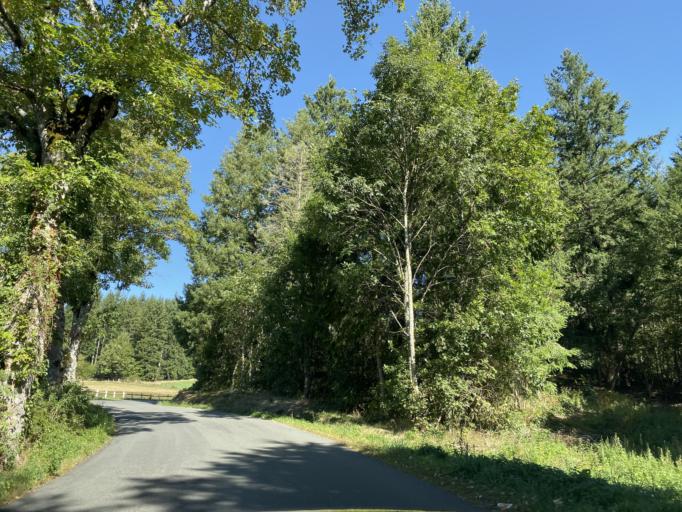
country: FR
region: Rhone-Alpes
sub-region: Departement de la Loire
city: Noiretable
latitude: 45.8234
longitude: 3.7705
